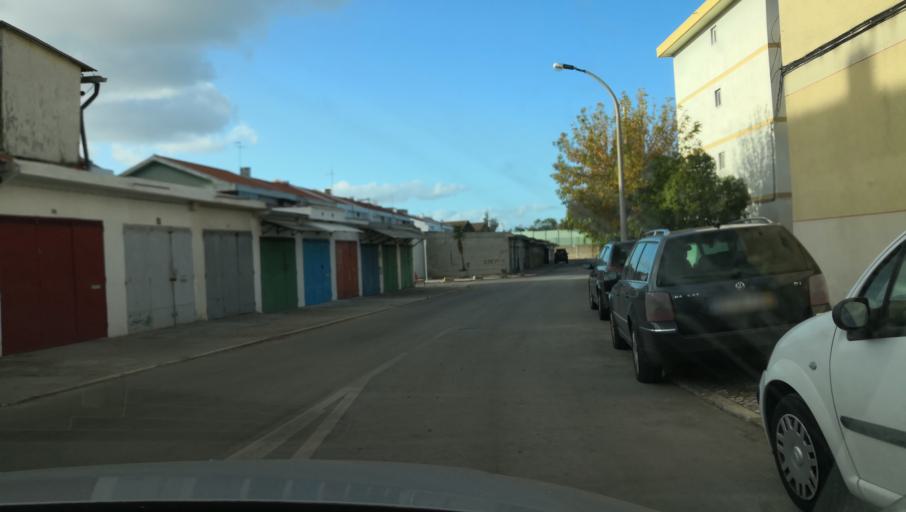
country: PT
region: Setubal
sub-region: Barreiro
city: Barreiro
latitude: 38.6705
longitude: -9.0489
